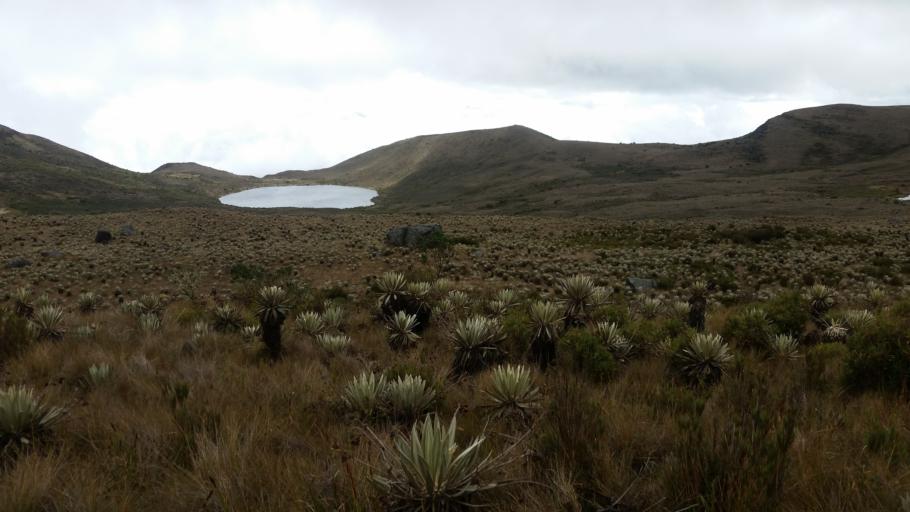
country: CO
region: Cundinamarca
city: Pasca
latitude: 4.3709
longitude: -74.2160
